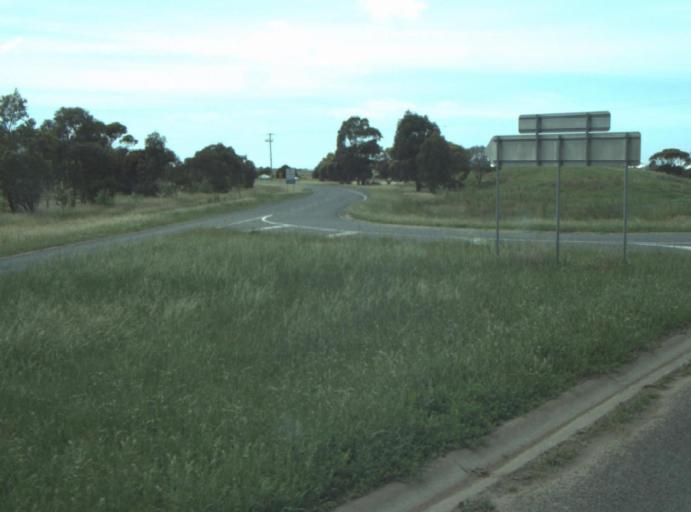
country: AU
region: Victoria
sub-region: Wyndham
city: Little River
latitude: -38.0119
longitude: 144.4653
